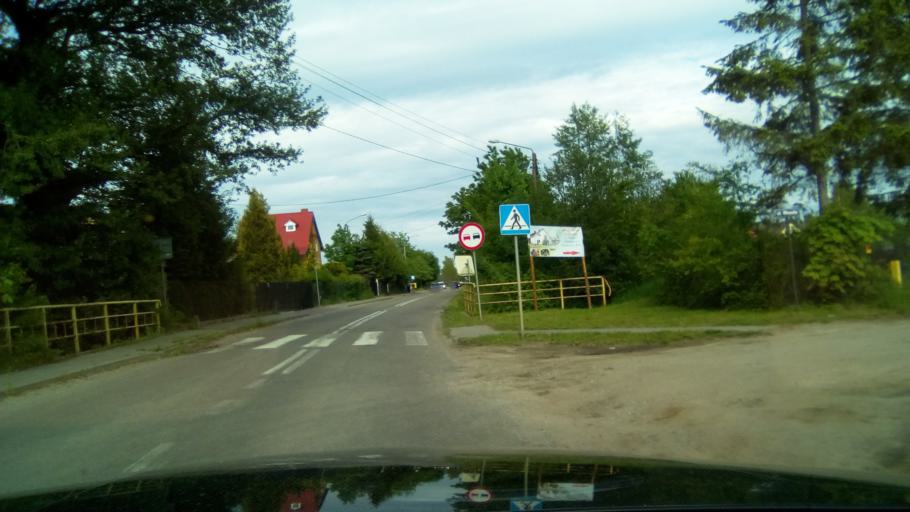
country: PL
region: Pomeranian Voivodeship
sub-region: Powiat pucki
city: Krokowa
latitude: 54.8102
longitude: 18.1960
